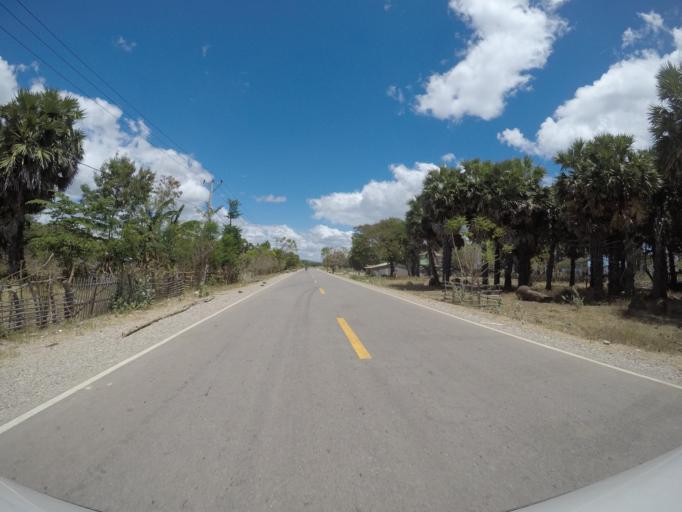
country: TL
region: Lautem
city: Lospalos
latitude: -8.3938
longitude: 126.8434
